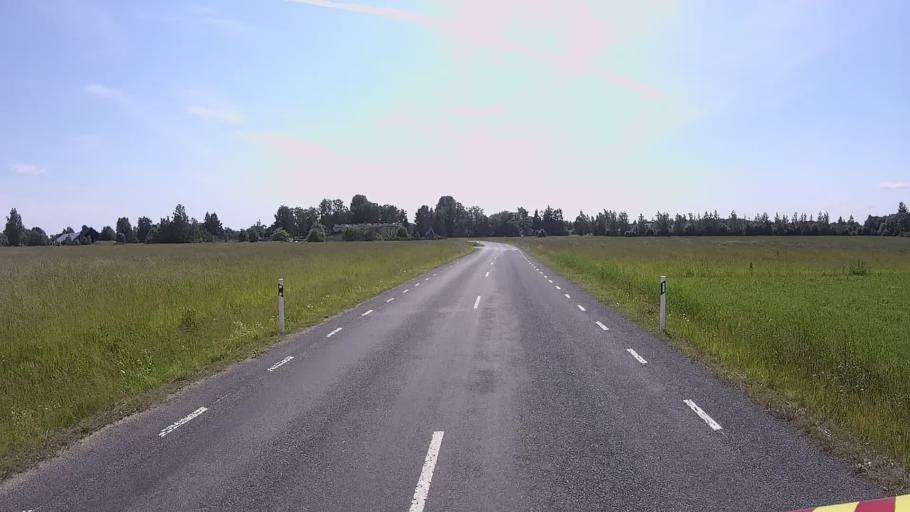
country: EE
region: Viljandimaa
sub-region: Karksi vald
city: Karksi-Nuia
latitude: 58.0676
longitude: 25.5522
